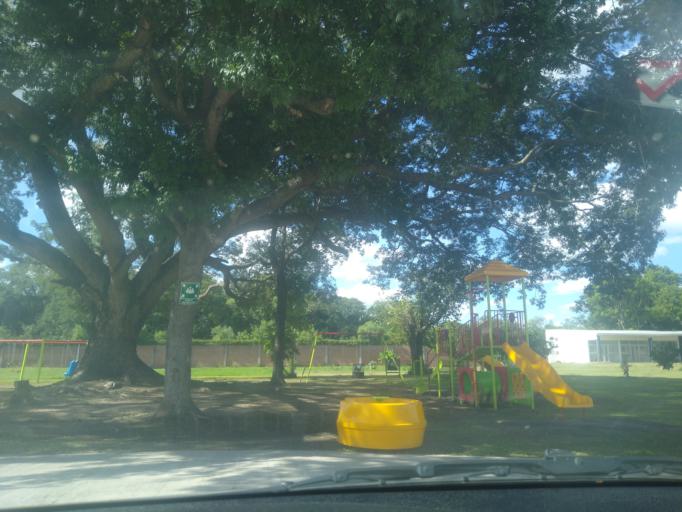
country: AR
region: Chaco
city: Resistencia
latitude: -27.4188
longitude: -58.9685
